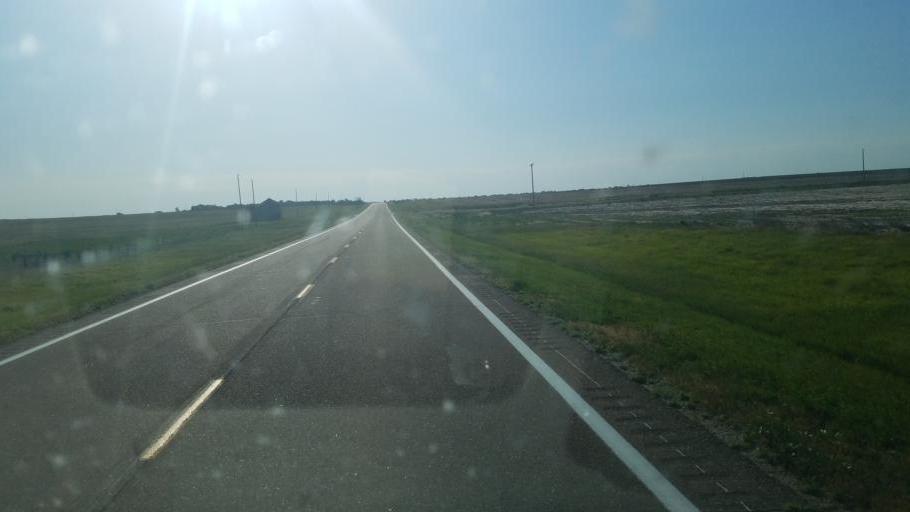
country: US
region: Kansas
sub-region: Edwards County
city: Kinsley
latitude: 38.1897
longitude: -99.4989
